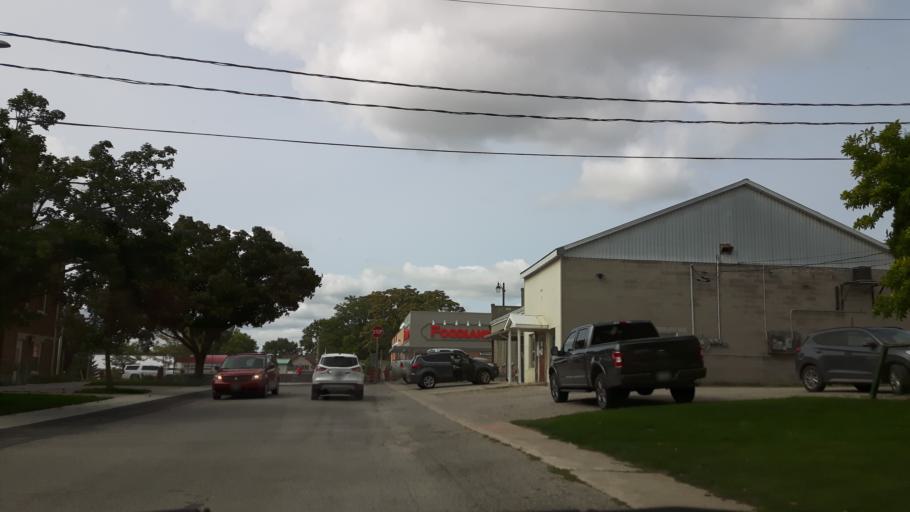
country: CA
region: Ontario
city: Huron East
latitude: 43.5504
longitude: -81.3949
